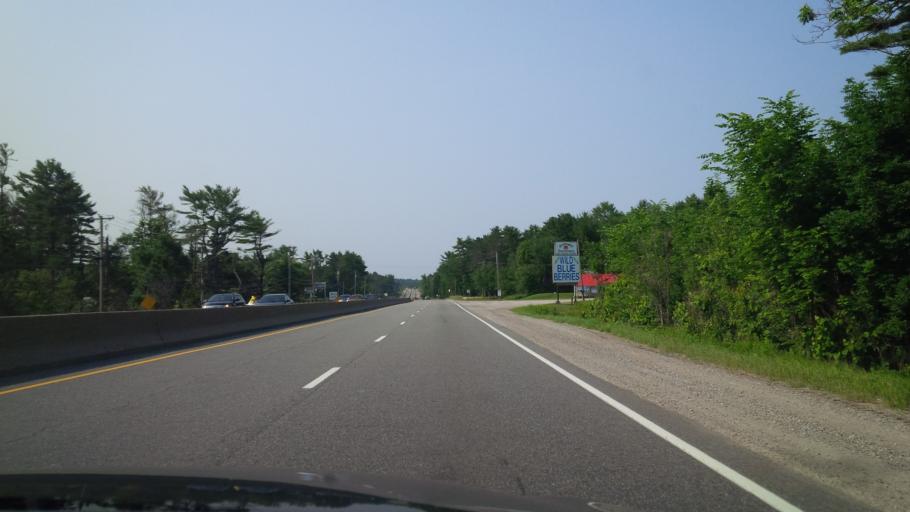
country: CA
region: Ontario
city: Gravenhurst
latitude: 44.8381
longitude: -79.3193
